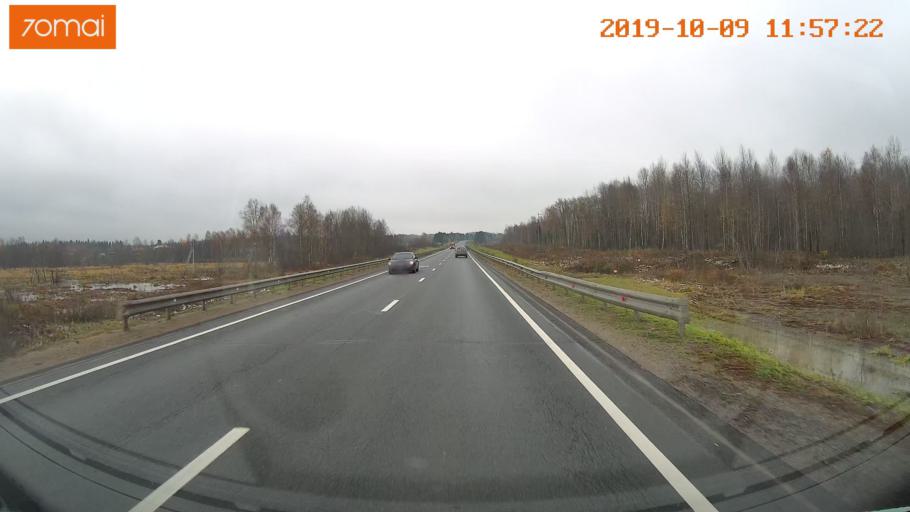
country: RU
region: Vologda
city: Gryazovets
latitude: 58.7330
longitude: 40.2922
